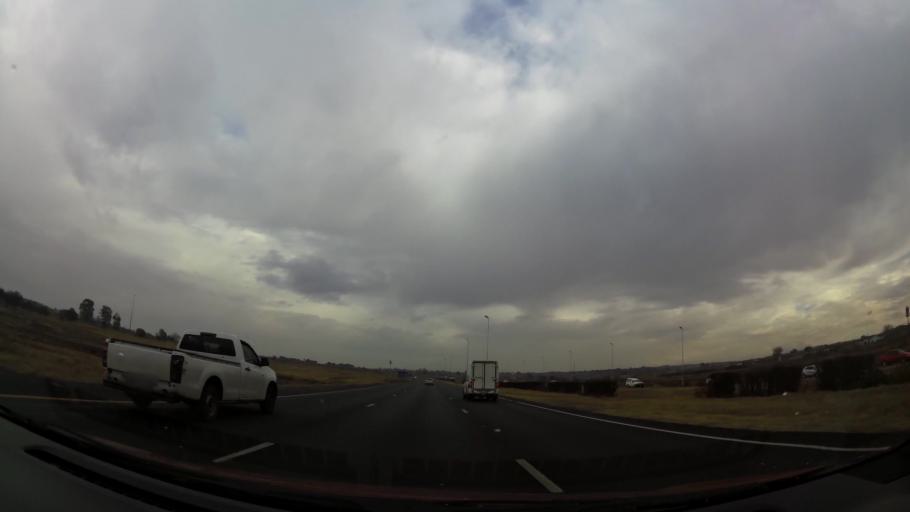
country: ZA
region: Gauteng
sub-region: City of Johannesburg Metropolitan Municipality
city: Soweto
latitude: -26.3041
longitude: 27.9343
